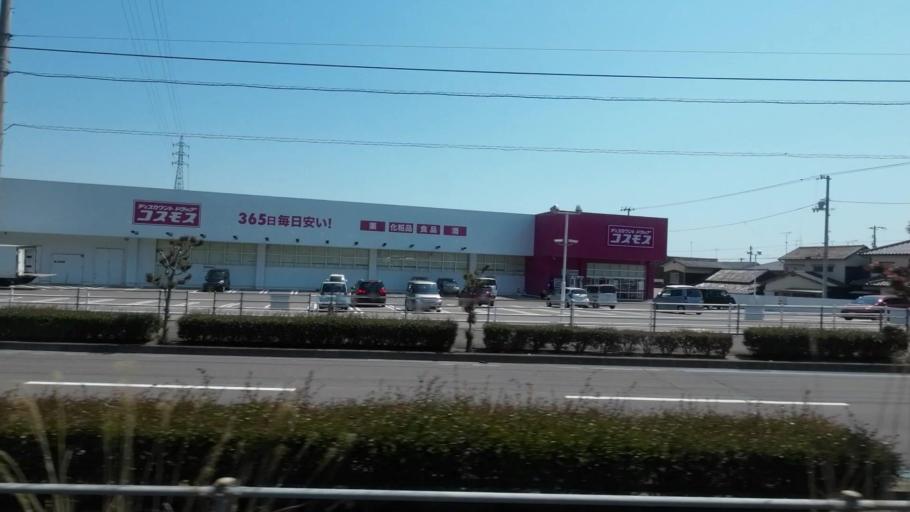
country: JP
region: Ehime
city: Hojo
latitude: 34.0737
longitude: 132.9862
